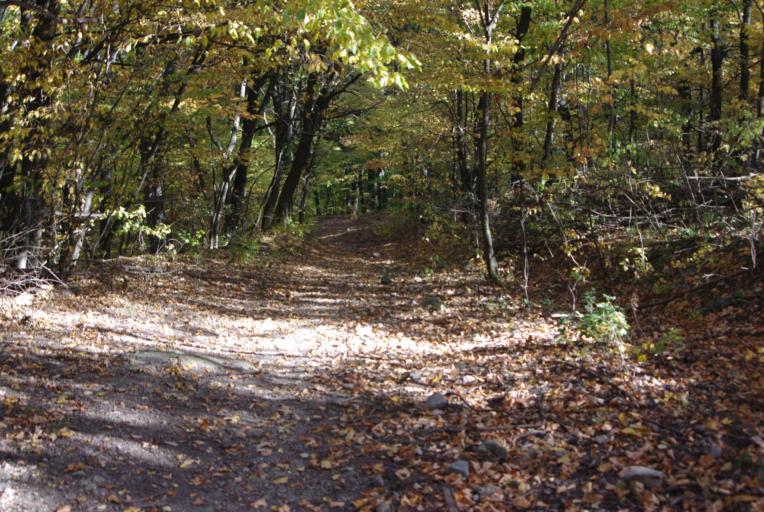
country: HU
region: Pest
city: Leanyfalu
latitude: 47.7361
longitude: 19.0557
